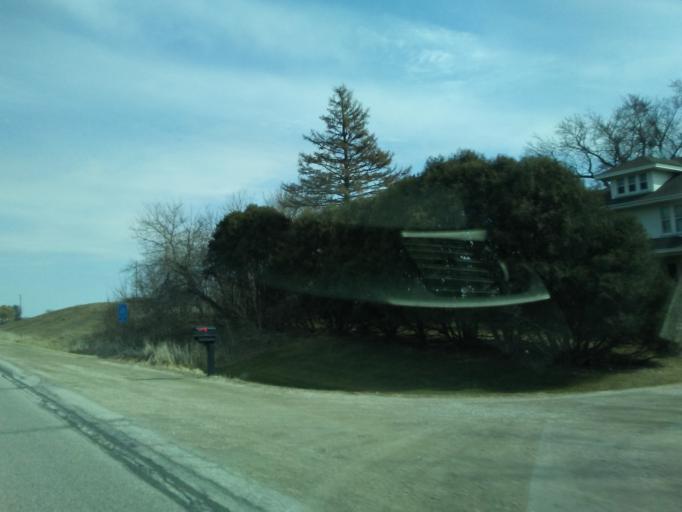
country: US
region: Iowa
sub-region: Allamakee County
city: Waukon
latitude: 43.2406
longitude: -91.5637
